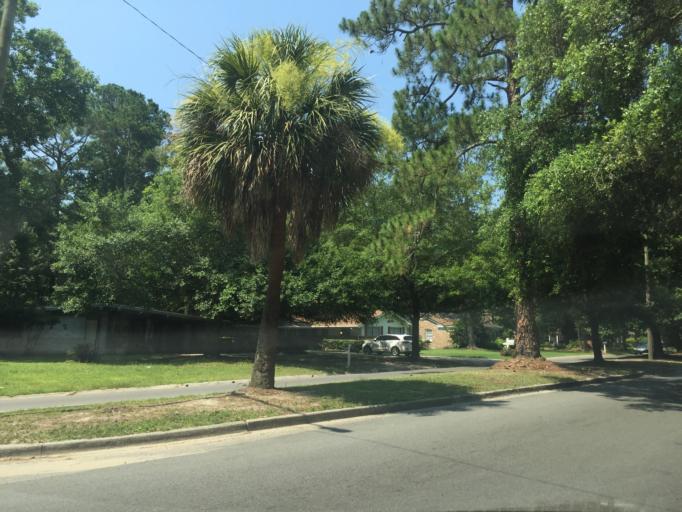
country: US
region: Georgia
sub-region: Chatham County
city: Montgomery
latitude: 31.9743
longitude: -81.1373
